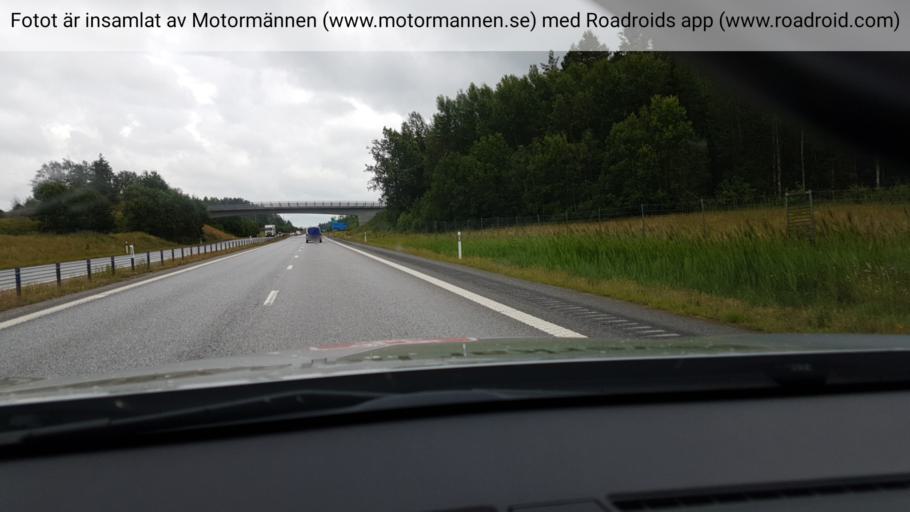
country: SE
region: Vaestra Goetaland
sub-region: Munkedals Kommun
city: Munkedal
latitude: 58.5324
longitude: 11.5359
